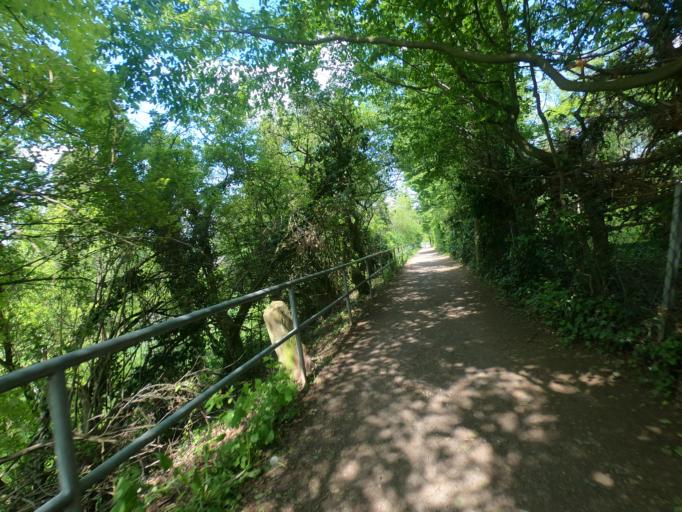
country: DE
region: Hesse
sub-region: Regierungsbezirk Darmstadt
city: Frankfurt am Main
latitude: 50.0868
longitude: 8.6853
